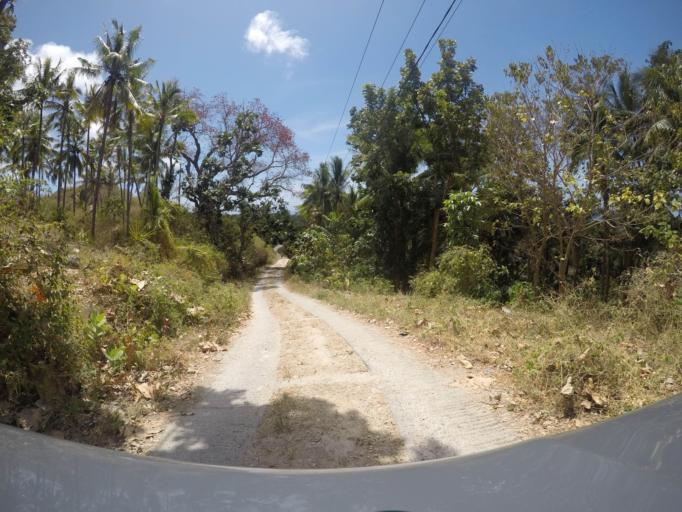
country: TL
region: Baucau
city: Baucau
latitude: -8.4528
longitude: 126.4414
